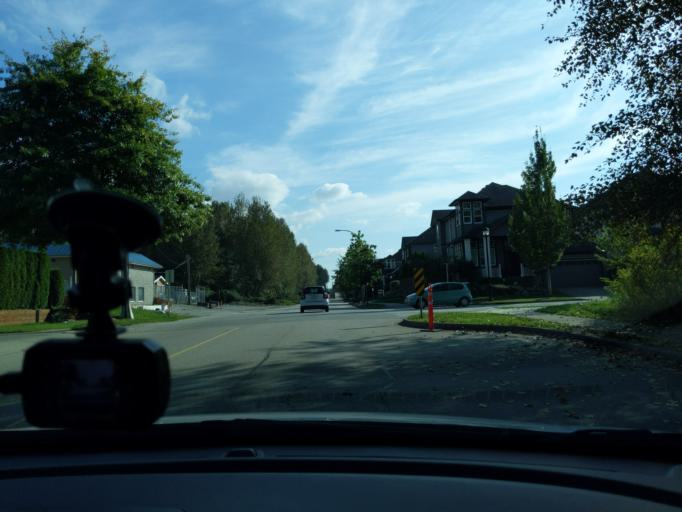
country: CA
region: British Columbia
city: Pitt Meadows
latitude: 49.2063
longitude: -122.6784
